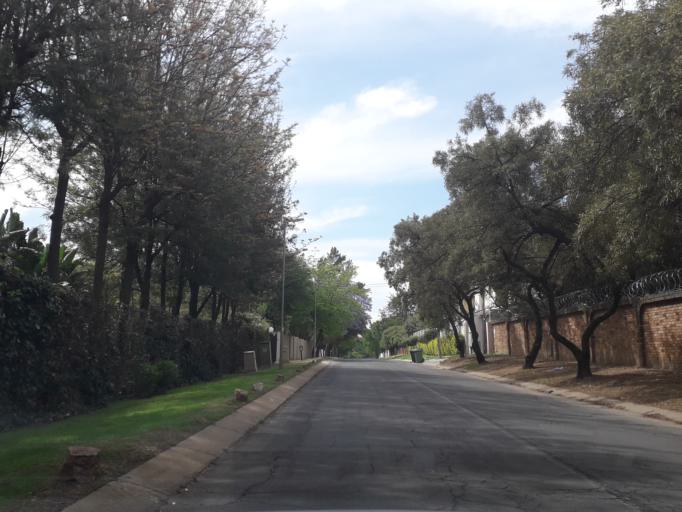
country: ZA
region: Gauteng
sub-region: City of Johannesburg Metropolitan Municipality
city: Diepsloot
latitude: -26.0630
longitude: 28.0178
